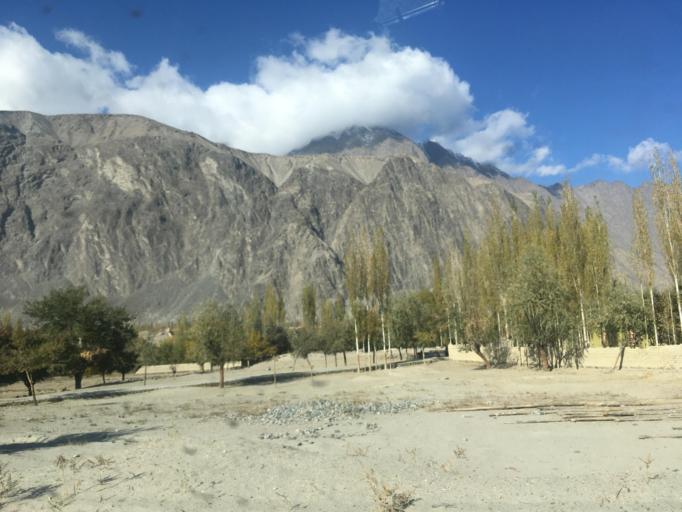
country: PK
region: Gilgit-Baltistan
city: Skardu
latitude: 35.3493
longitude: 75.5236
